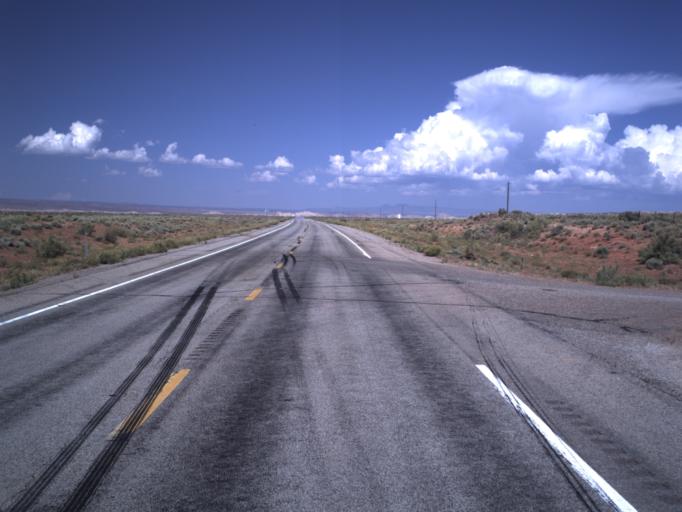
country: US
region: Utah
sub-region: San Juan County
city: Blanding
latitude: 37.1713
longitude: -109.5807
